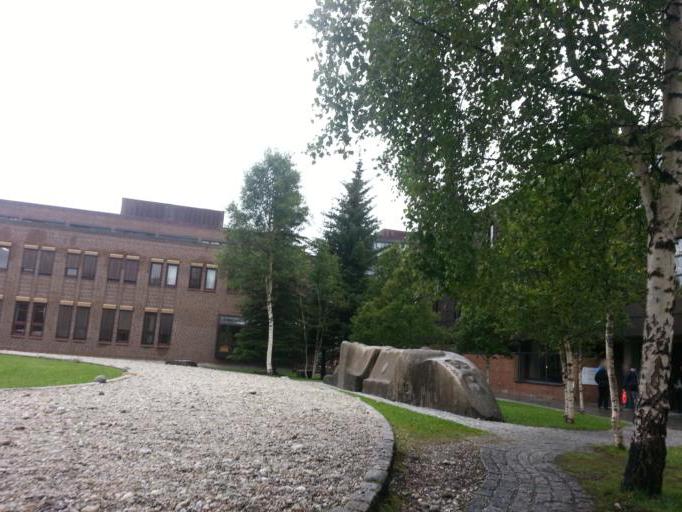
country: NO
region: Troms
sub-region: Tromso
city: Tromso
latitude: 69.6806
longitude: 18.9730
